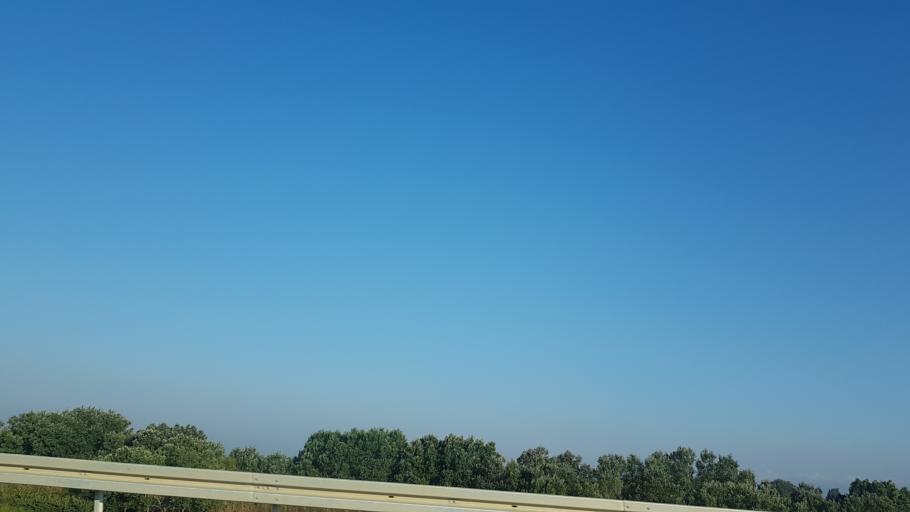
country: TR
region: Bursa
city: Karacabey
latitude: 40.1805
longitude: 28.3295
